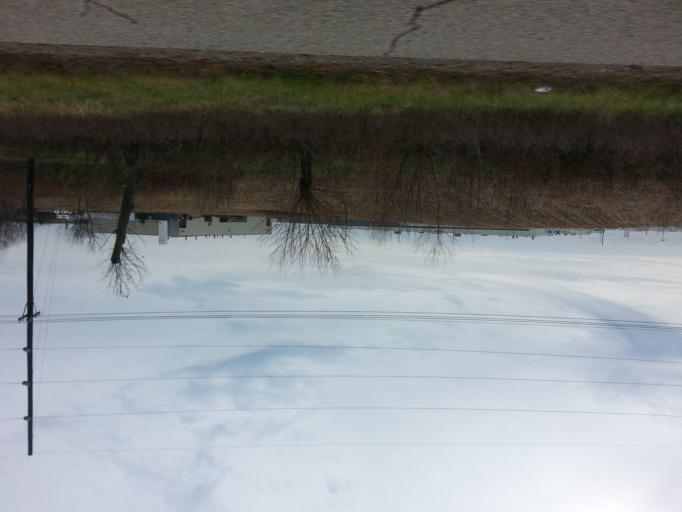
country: US
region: Indiana
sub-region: Decatur County
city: Greensburg
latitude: 39.3577
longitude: -85.4619
